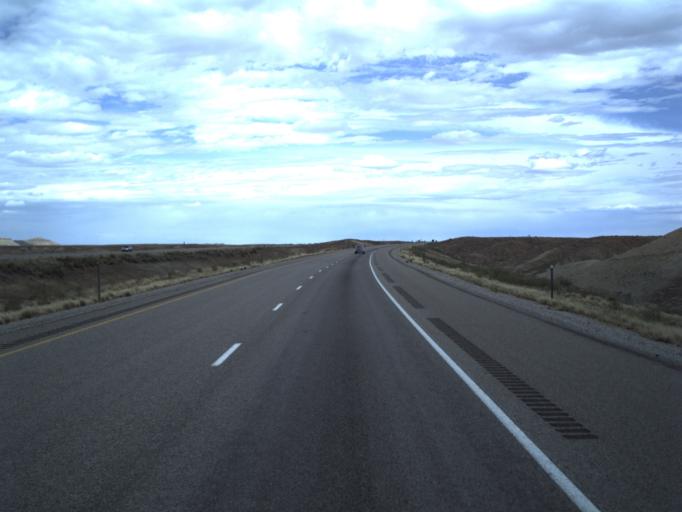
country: US
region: Utah
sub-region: Grand County
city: Moab
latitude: 38.9256
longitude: -109.9866
